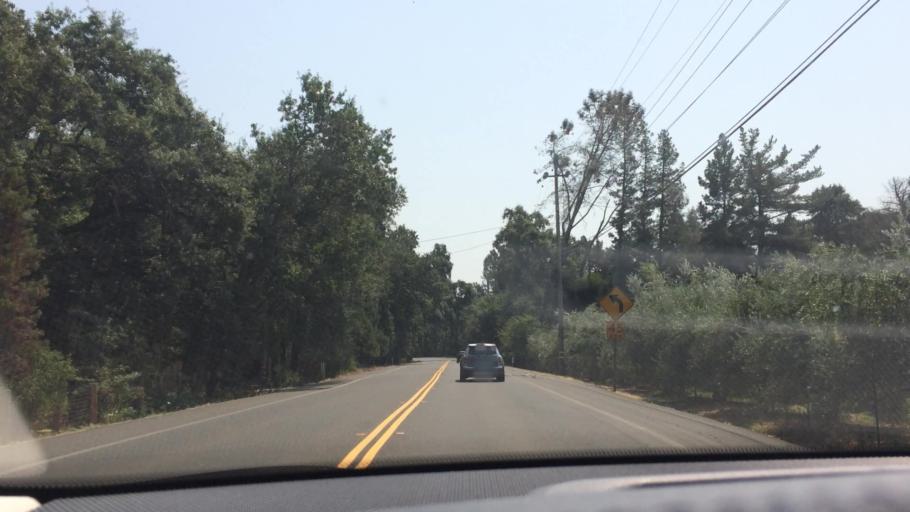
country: US
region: California
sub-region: Napa County
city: Deer Park
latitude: 38.5586
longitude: -122.5061
